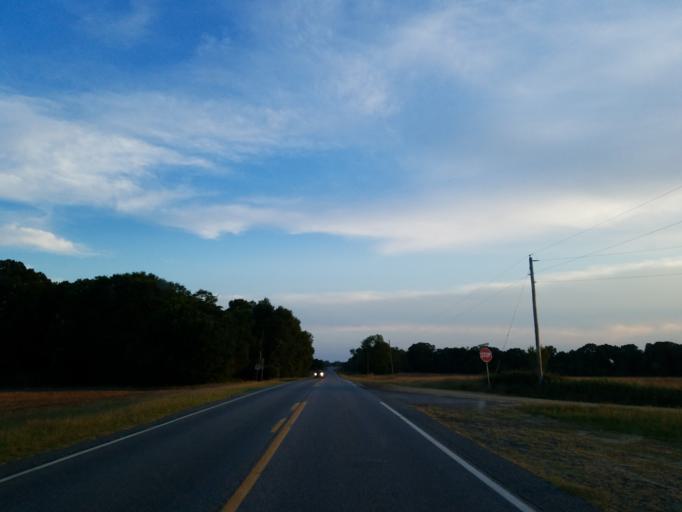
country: US
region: Georgia
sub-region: Crisp County
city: Cordele
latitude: 31.8309
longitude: -83.7886
